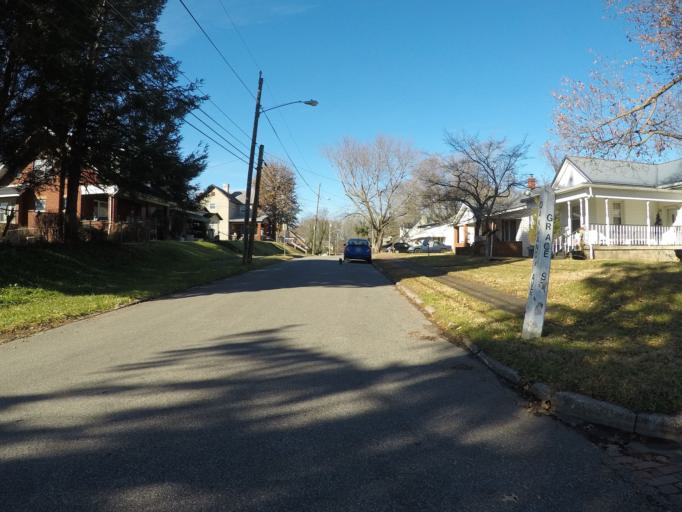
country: US
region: West Virginia
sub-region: Cabell County
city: Huntington
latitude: 38.4093
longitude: -82.4087
